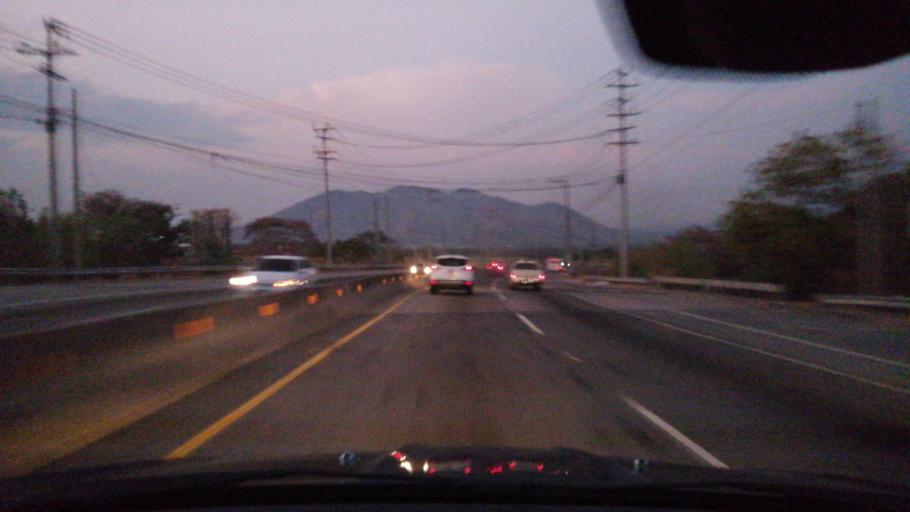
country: SV
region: San Salvador
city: Ayutuxtepeque
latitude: 13.7685
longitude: -89.2127
